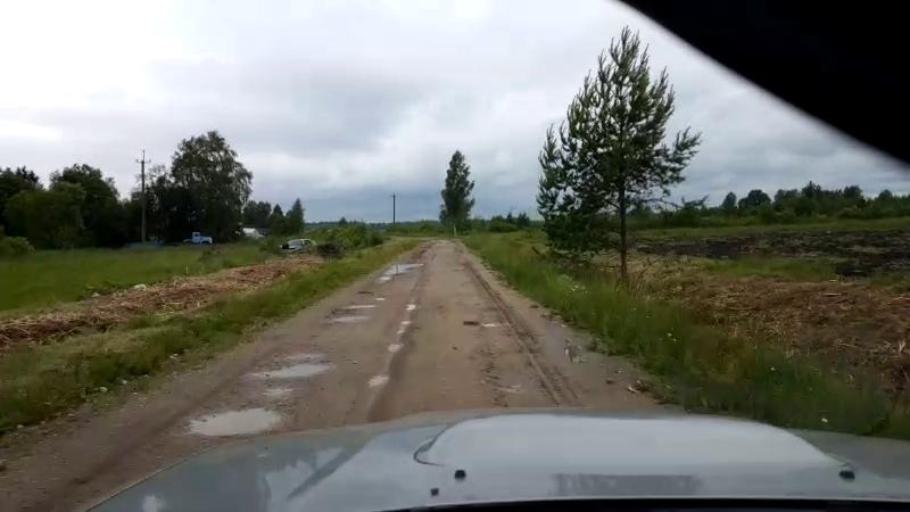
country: EE
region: Paernumaa
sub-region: Halinga vald
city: Parnu-Jaagupi
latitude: 58.5337
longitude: 24.5825
